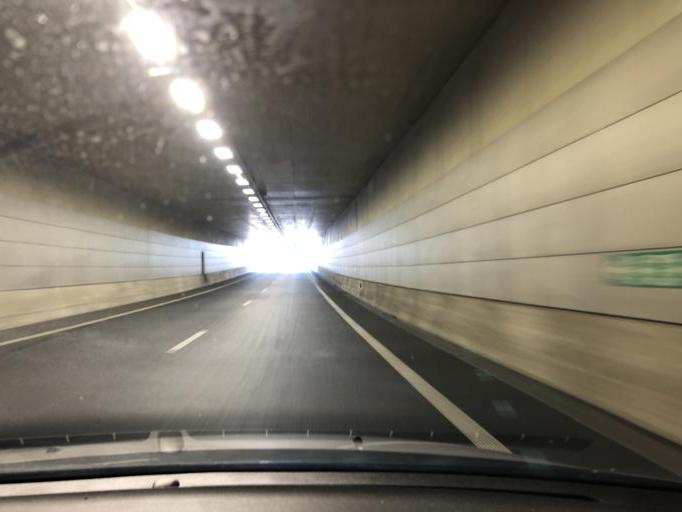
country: NL
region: North Holland
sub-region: Gemeente Medemblik
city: Medemblik
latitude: 52.6862
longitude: 5.1617
